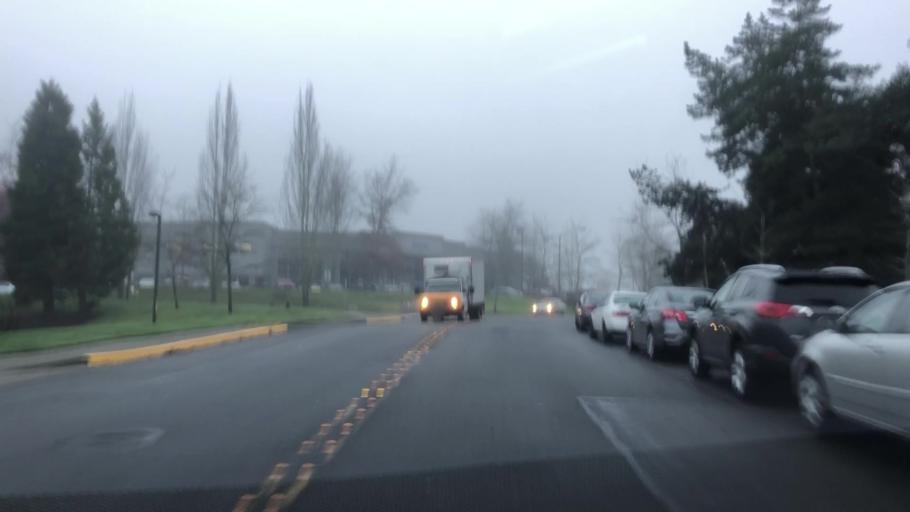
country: US
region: Washington
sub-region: King County
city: Sammamish
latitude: 47.6646
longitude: -122.0937
